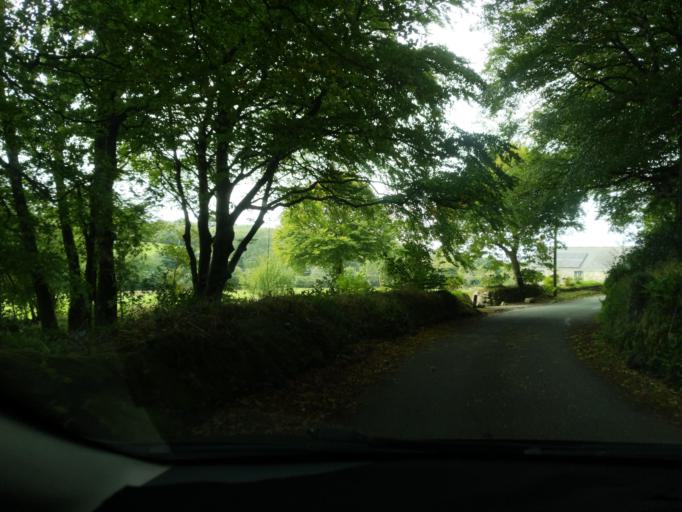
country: GB
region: England
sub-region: Cornwall
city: Lostwithiel
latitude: 50.4000
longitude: -4.6937
